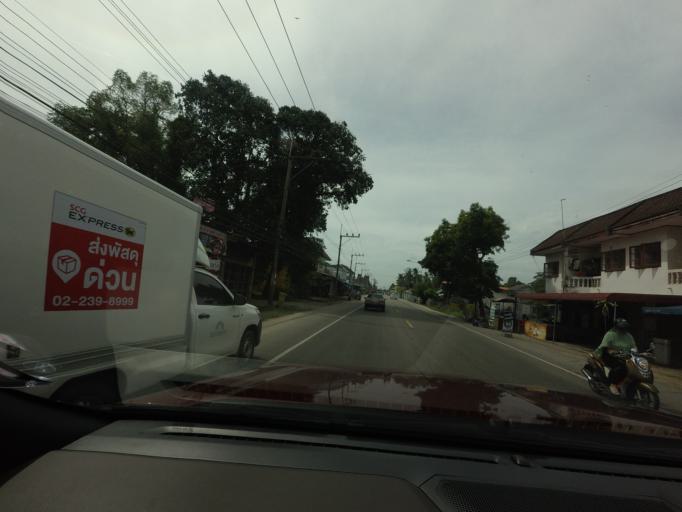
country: TH
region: Narathiwat
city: Tak Bai
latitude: 6.2397
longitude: 102.0810
